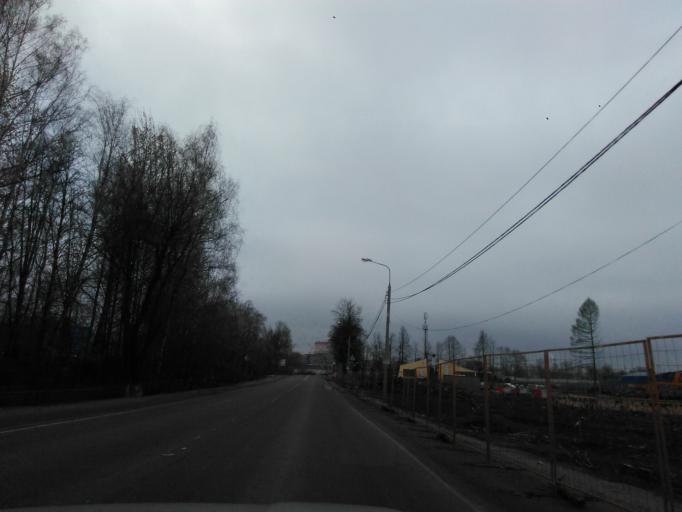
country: RU
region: Moskovskaya
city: Nakhabino
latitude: 55.8427
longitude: 37.1698
